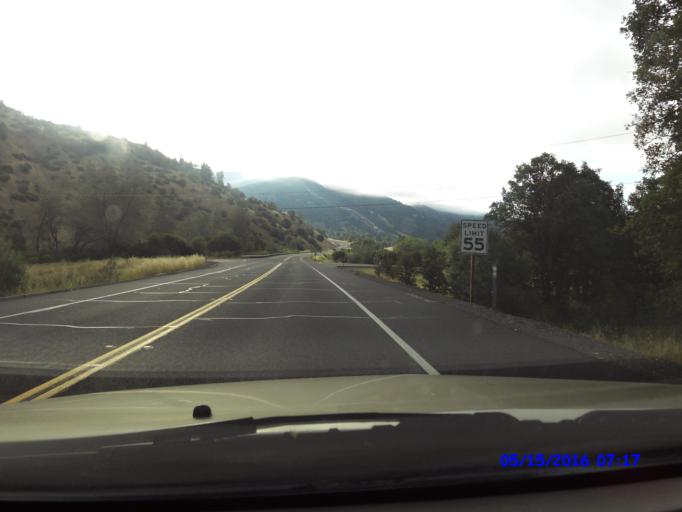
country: US
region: California
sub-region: Tuolumne County
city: Tuolumne City
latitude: 37.8148
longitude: -120.3130
